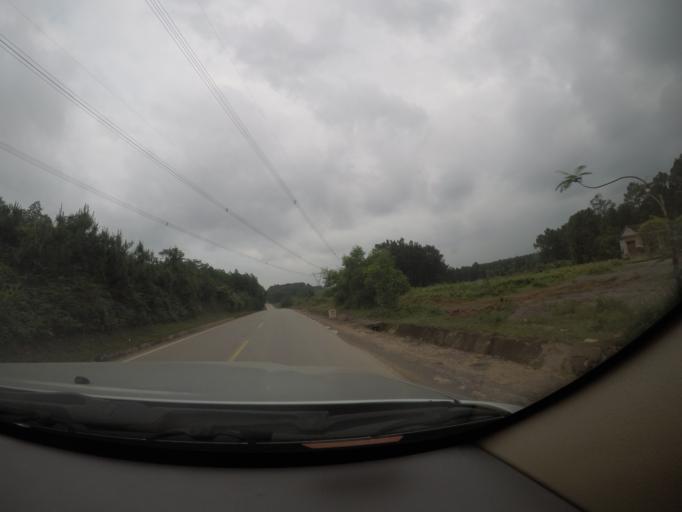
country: VN
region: Quang Binh
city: Kien Giang
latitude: 17.1514
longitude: 106.7523
